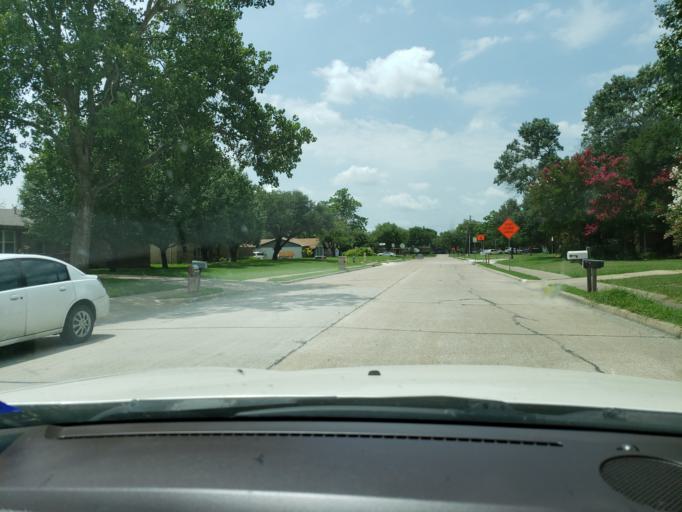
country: US
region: Texas
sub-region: Dallas County
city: Rowlett
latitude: 32.8956
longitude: -96.5630
